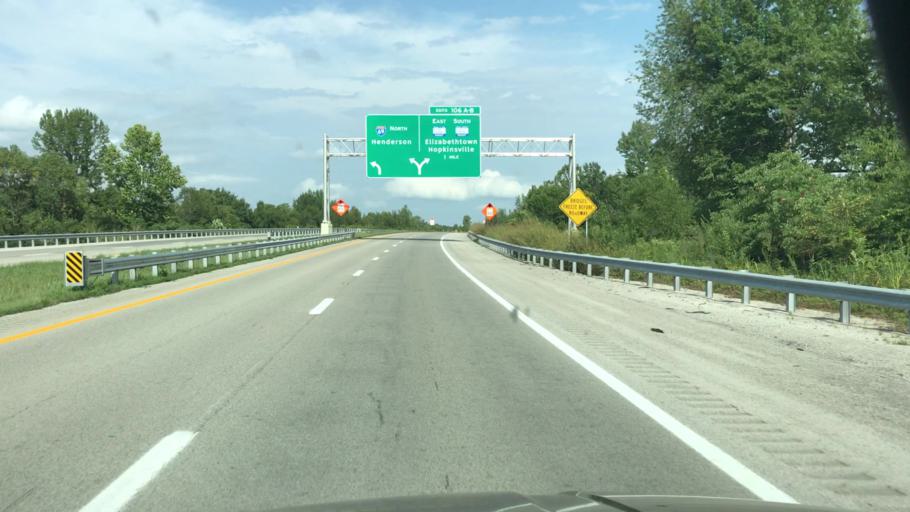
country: US
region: Kentucky
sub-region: Hopkins County
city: Nortonville
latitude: 37.2123
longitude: -87.4720
